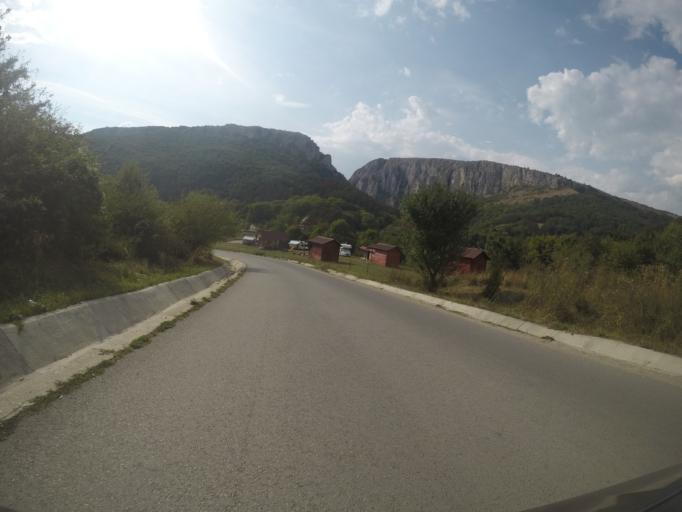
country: RO
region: Cluj
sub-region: Comuna Sandulesti
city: Sandulesti
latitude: 46.5598
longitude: 23.6943
